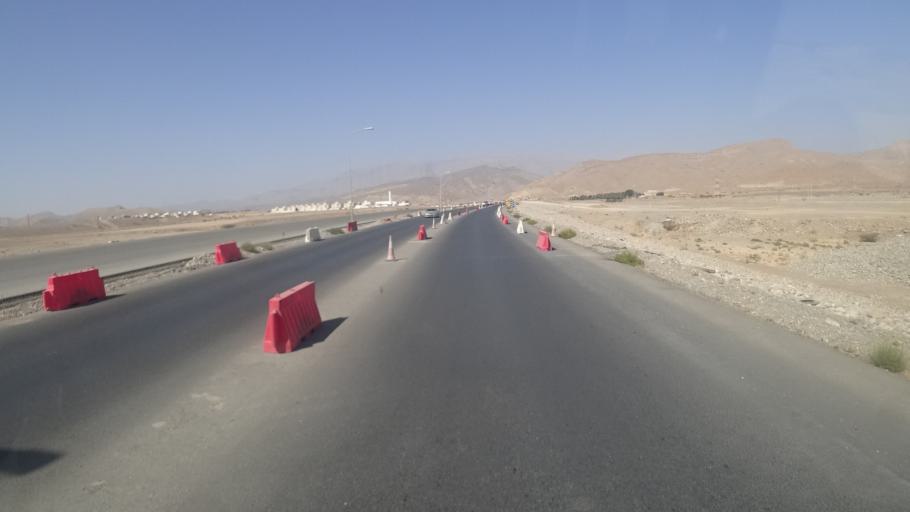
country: OM
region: Ash Sharqiyah
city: Sur
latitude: 22.5172
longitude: 59.4522
